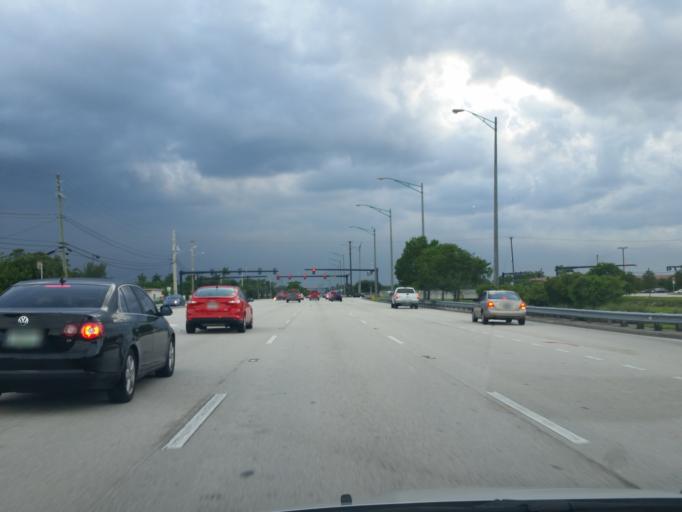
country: US
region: Florida
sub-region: Broward County
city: Cooper City
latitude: 26.0646
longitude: -80.2584
